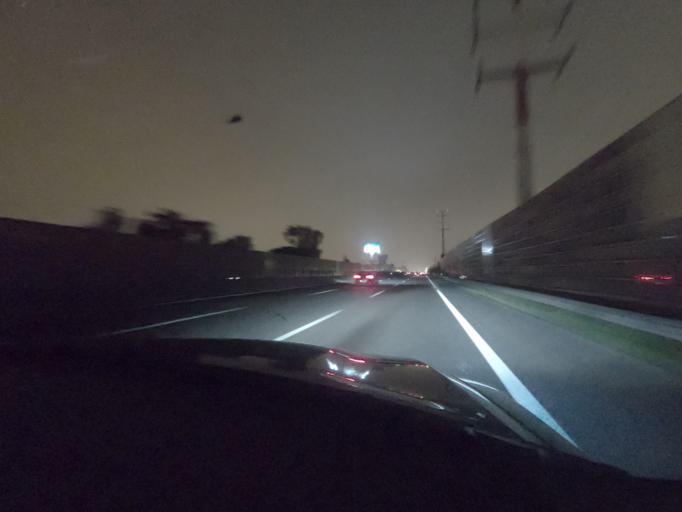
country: PT
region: Lisbon
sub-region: Loures
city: Sao Joao da Talha
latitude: 38.8295
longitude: -9.0977
